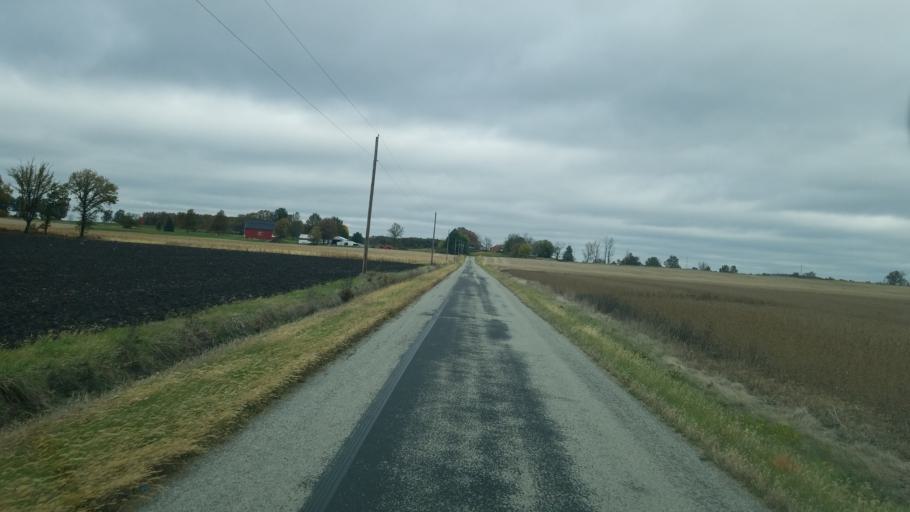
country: US
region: Ohio
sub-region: Huron County
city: Willard
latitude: 40.9406
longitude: -82.8117
